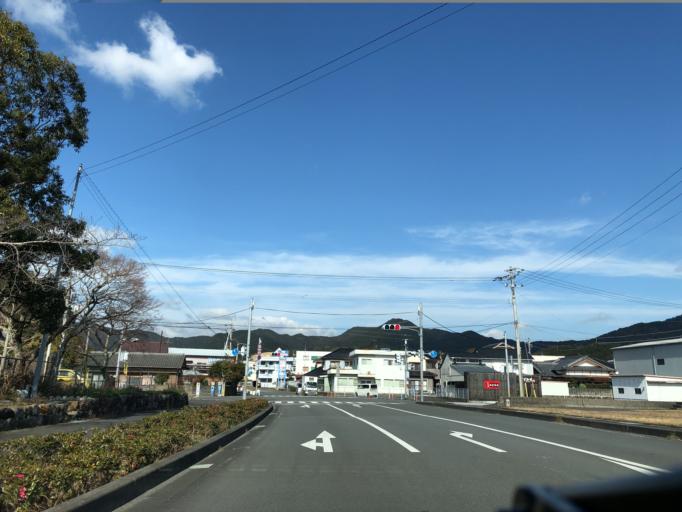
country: JP
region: Kochi
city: Sukumo
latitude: 32.9247
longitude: 132.7028
